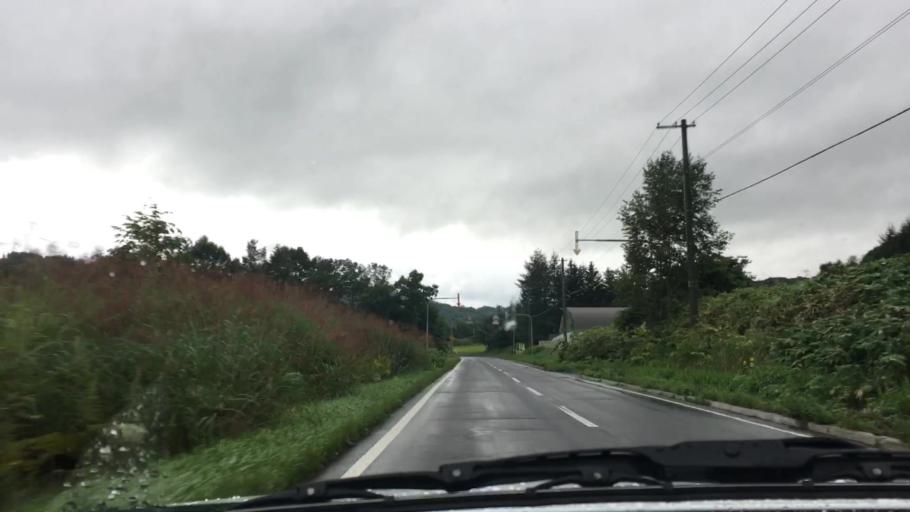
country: JP
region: Hokkaido
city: Niseko Town
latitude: 42.6538
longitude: 140.7396
